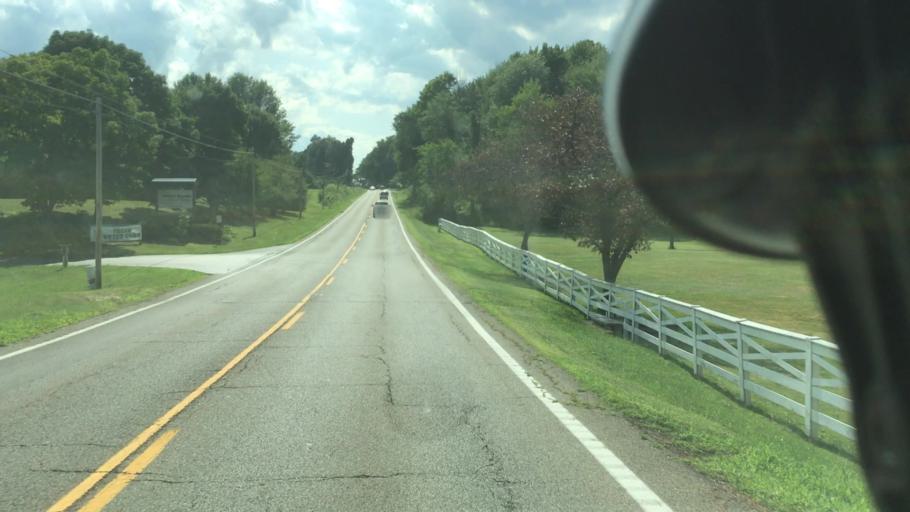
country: US
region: Ohio
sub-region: Mahoning County
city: Canfield
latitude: 40.9867
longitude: -80.8053
